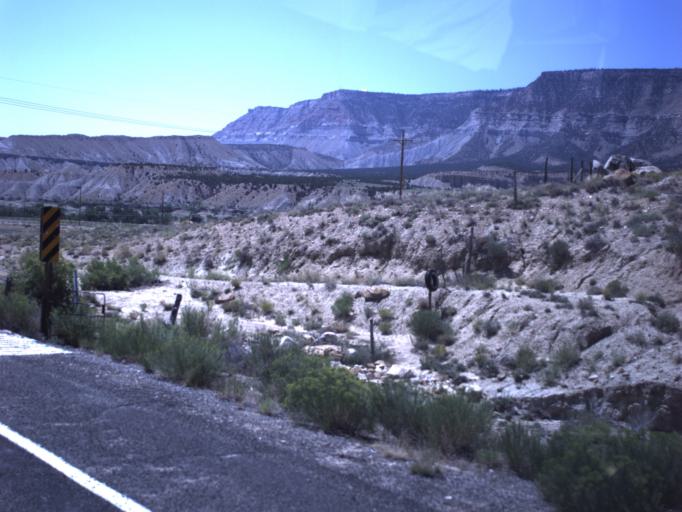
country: US
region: Utah
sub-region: Emery County
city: Orangeville
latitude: 39.2599
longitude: -111.0985
